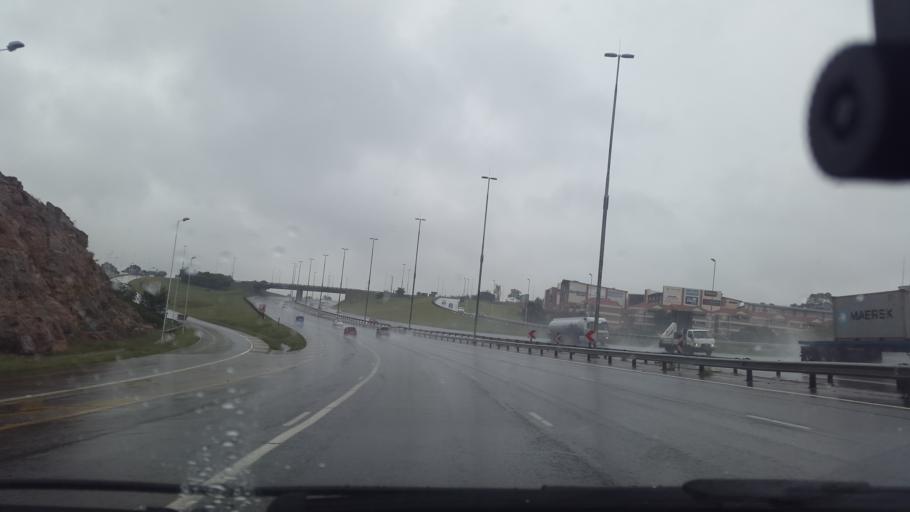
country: ZA
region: Gauteng
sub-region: City of Johannesburg Metropolitan Municipality
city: Johannesburg
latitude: -26.2602
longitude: 28.0121
